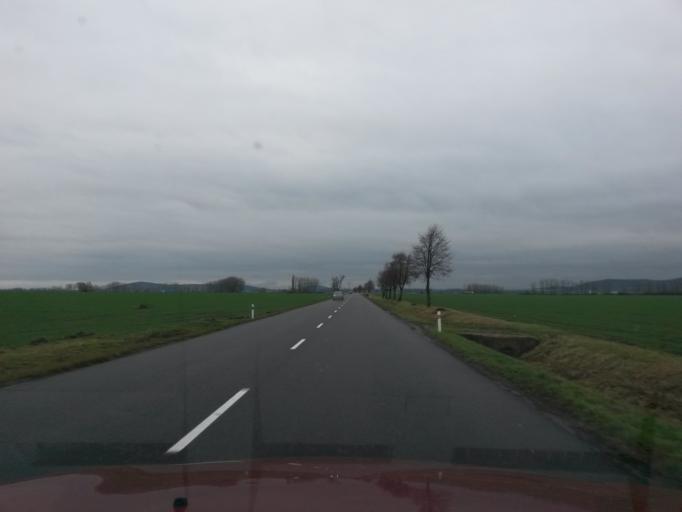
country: SK
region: Kosicky
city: Trebisov
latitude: 48.5533
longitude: 21.6806
